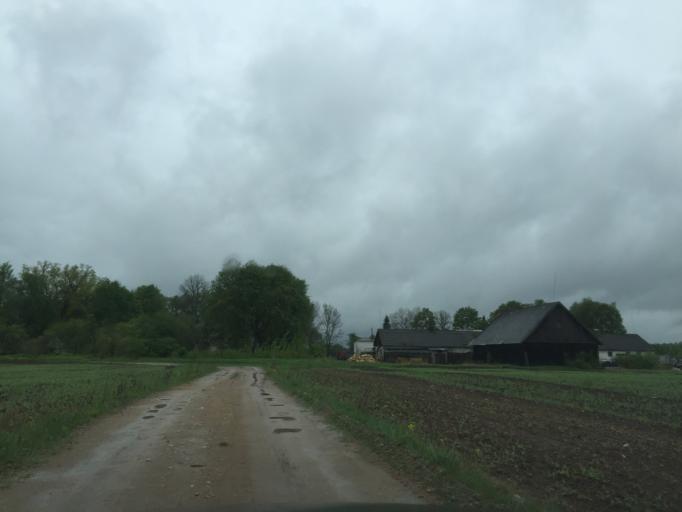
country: LV
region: Ogre
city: Jumprava
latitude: 56.6626
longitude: 25.0070
